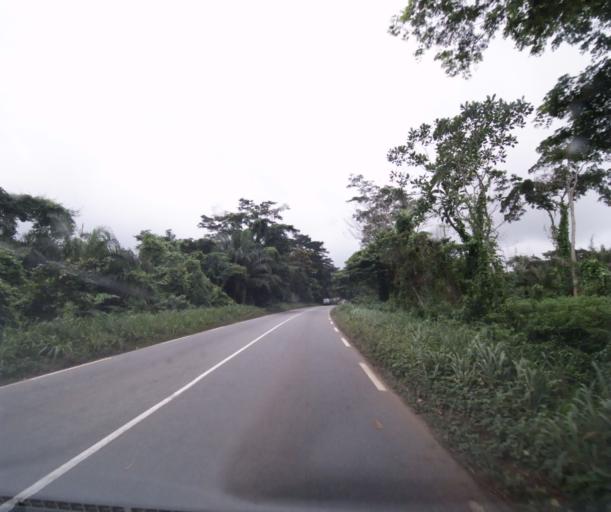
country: CM
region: Centre
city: Eseka
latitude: 3.8734
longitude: 10.6702
